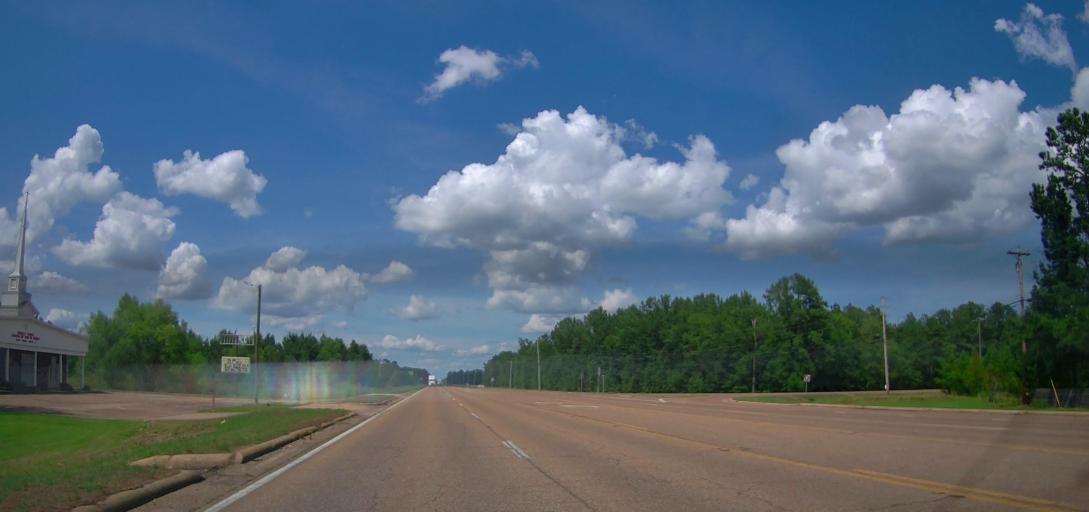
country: US
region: Mississippi
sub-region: Lowndes County
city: Columbus Air Force Base
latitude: 33.5717
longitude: -88.4311
